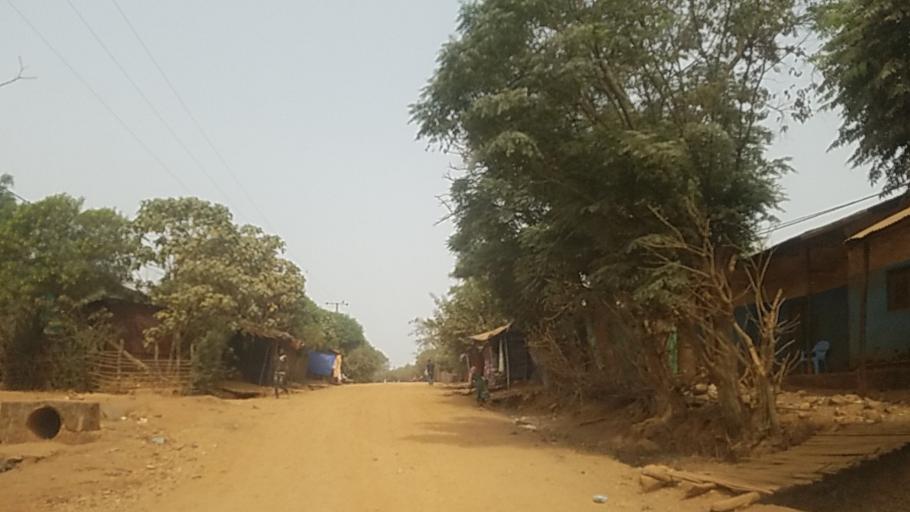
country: ET
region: Amhara
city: Bure
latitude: 10.7754
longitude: 36.2644
